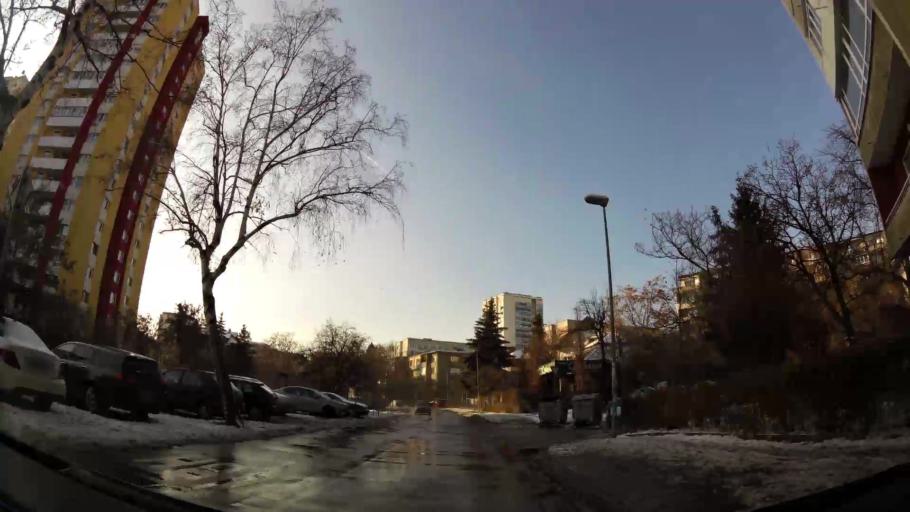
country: BG
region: Sofia-Capital
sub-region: Stolichna Obshtina
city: Sofia
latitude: 42.6695
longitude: 23.3573
